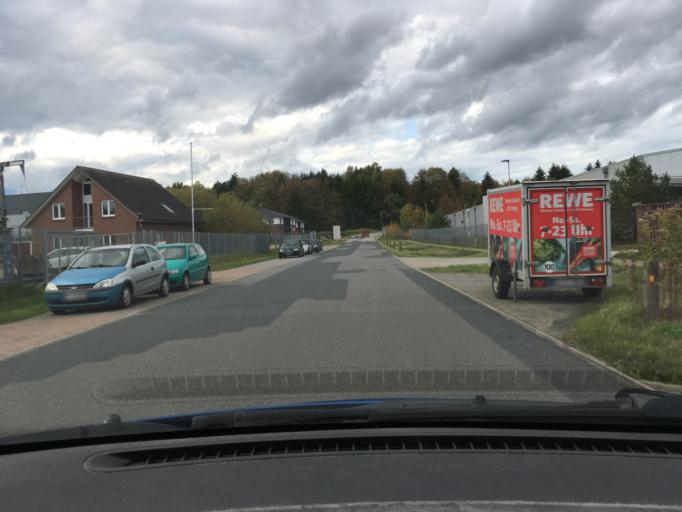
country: DE
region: Lower Saxony
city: Buchholz in der Nordheide
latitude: 53.3728
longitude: 9.8921
